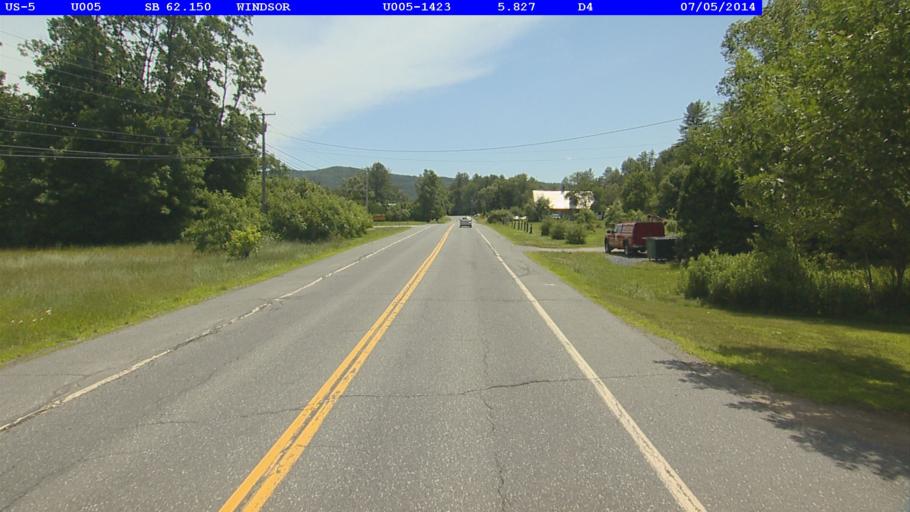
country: US
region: Vermont
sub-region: Windsor County
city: Windsor
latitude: 43.5063
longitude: -72.4013
